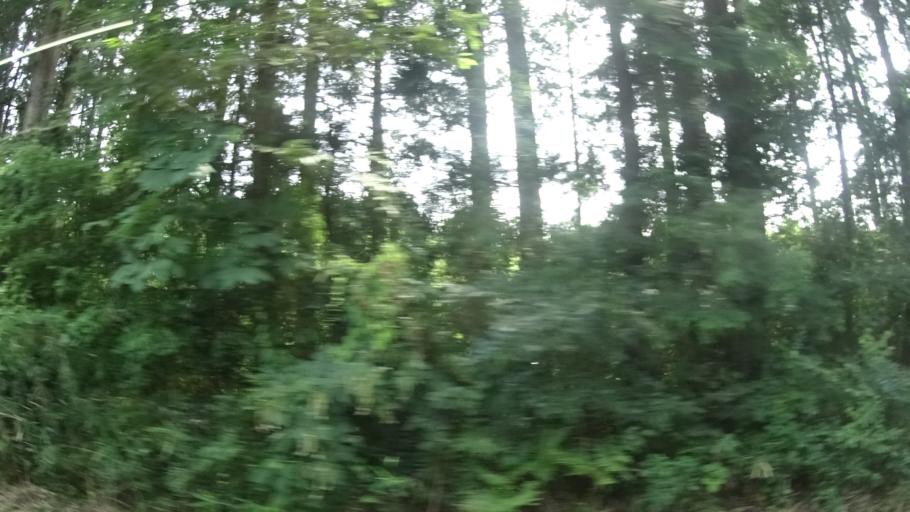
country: JP
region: Tochigi
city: Kanuma
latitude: 36.6344
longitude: 139.7292
